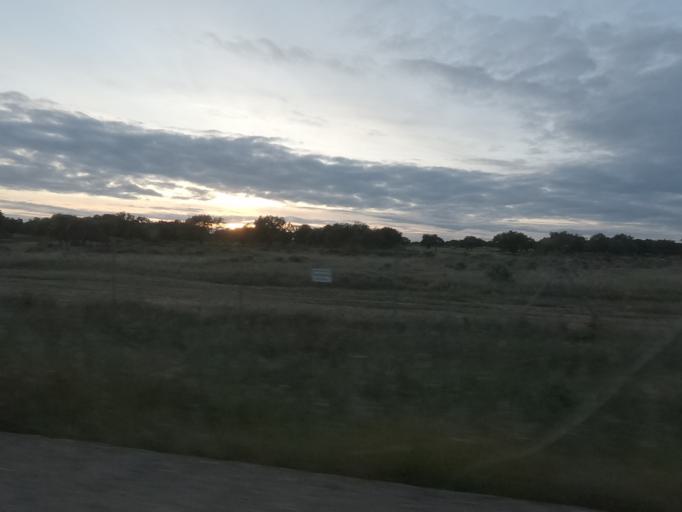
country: ES
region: Extremadura
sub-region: Provincia de Badajoz
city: Villar del Rey
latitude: 38.9963
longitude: -6.8696
